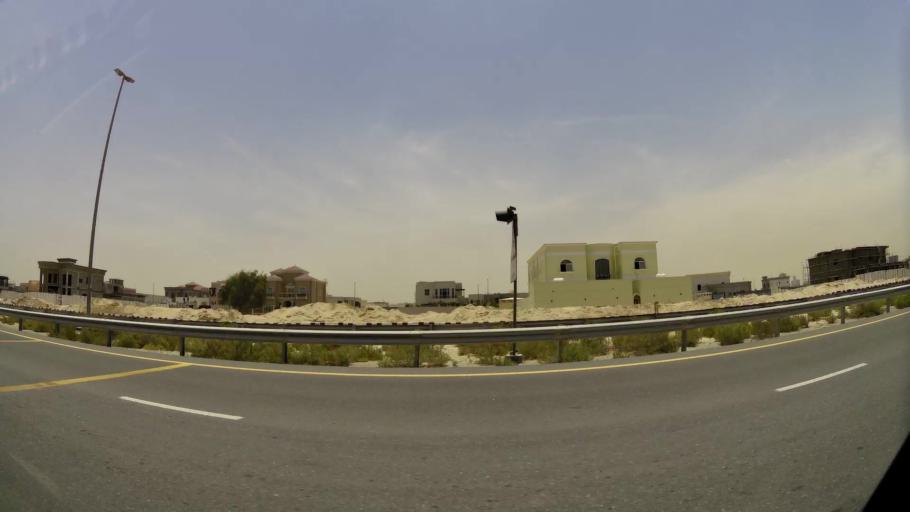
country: AE
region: Dubai
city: Dubai
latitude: 25.0724
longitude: 55.2178
